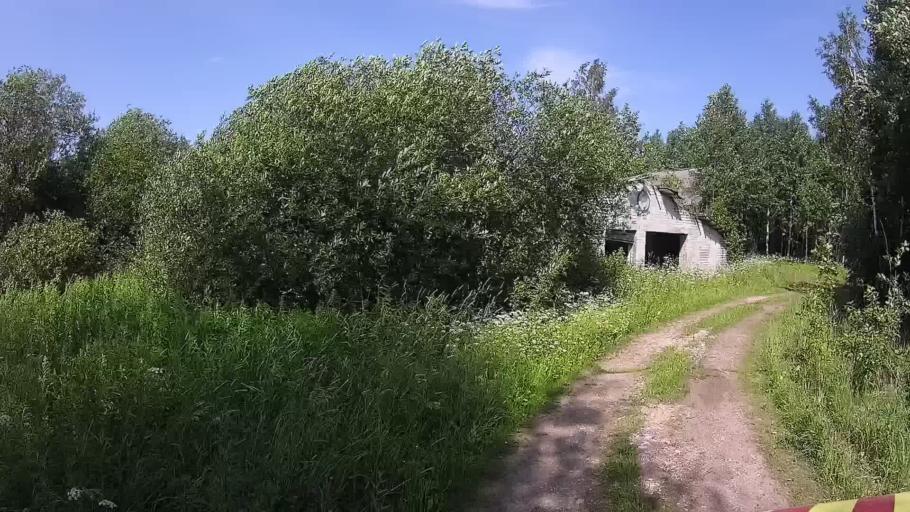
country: EE
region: Viljandimaa
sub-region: Karksi vald
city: Karksi-Nuia
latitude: 58.0047
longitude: 25.5130
